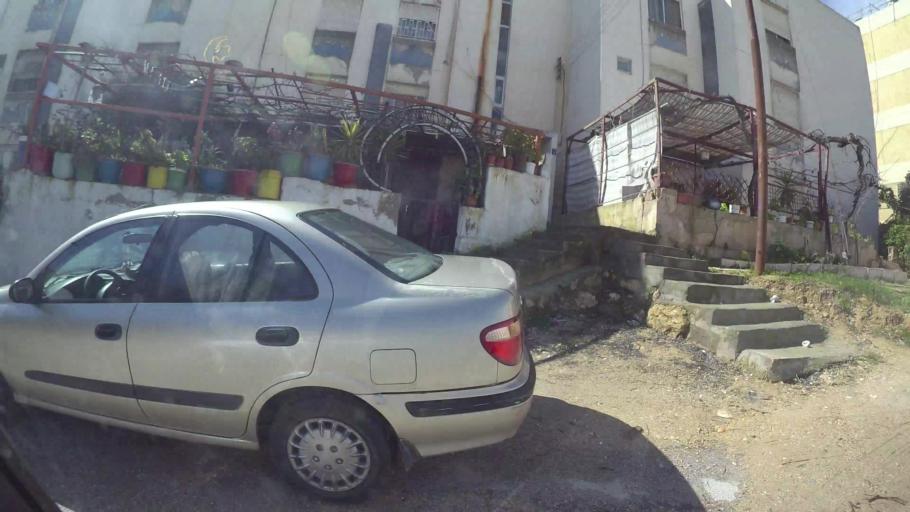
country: JO
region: Amman
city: Al Jubayhah
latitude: 32.0560
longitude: 35.8831
